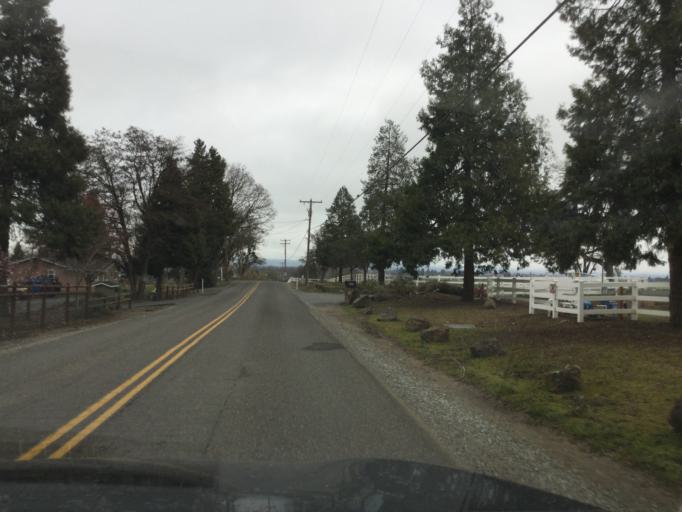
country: US
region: Oregon
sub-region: Jackson County
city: Central Point
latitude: 42.3902
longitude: -122.9595
